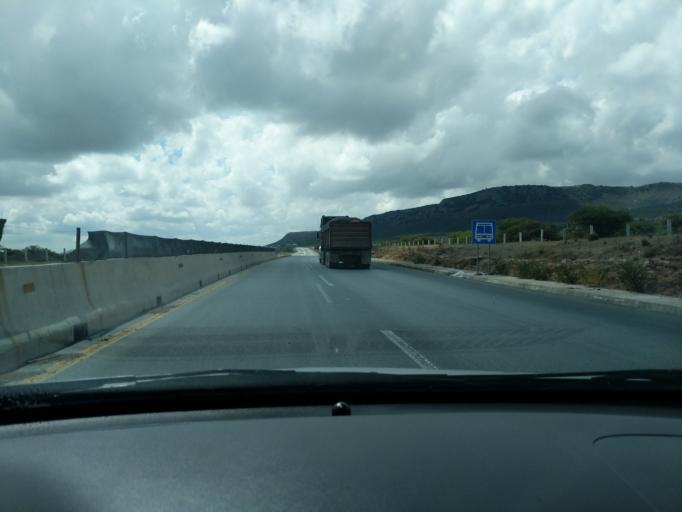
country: MX
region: Zacatecas
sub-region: Pinos
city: Santiago
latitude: 22.4060
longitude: -101.3899
